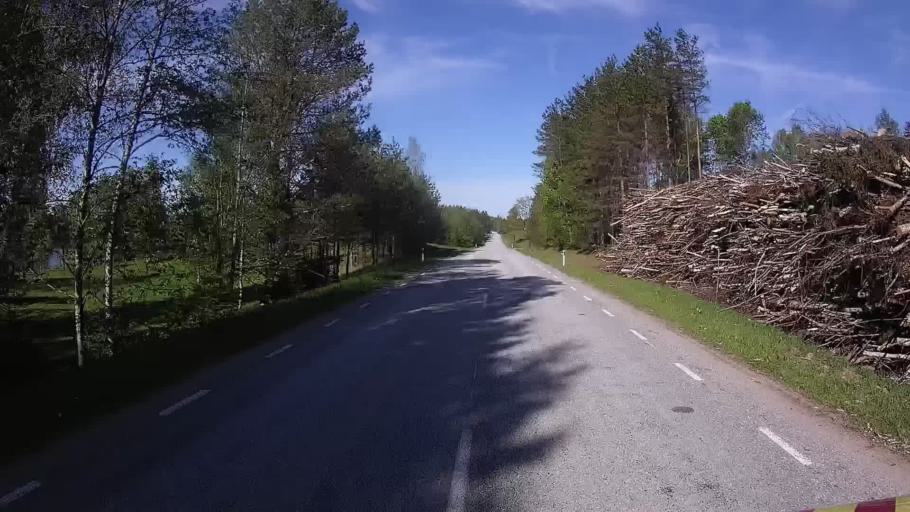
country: EE
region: Vorumaa
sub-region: Antsla vald
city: Vana-Antsla
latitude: 57.9879
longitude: 26.4821
